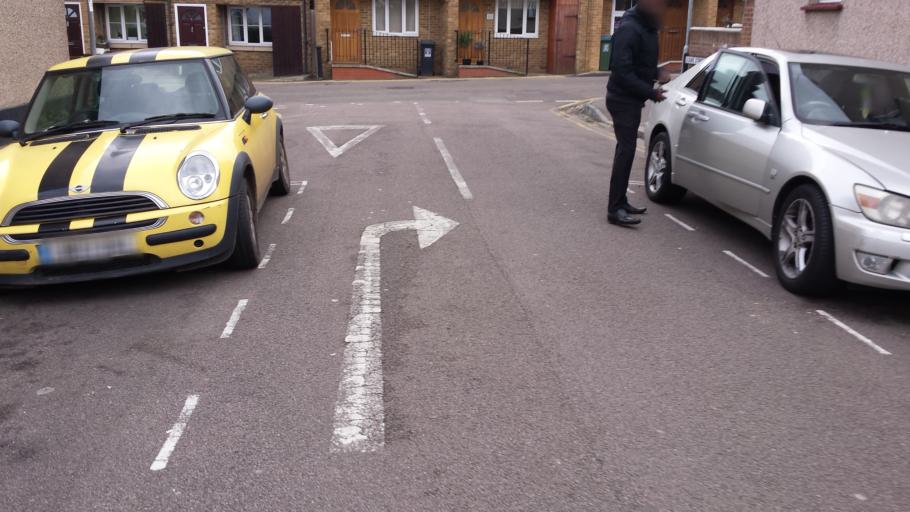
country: GB
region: England
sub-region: Hertfordshire
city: Watford
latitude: 51.6581
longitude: -0.3933
